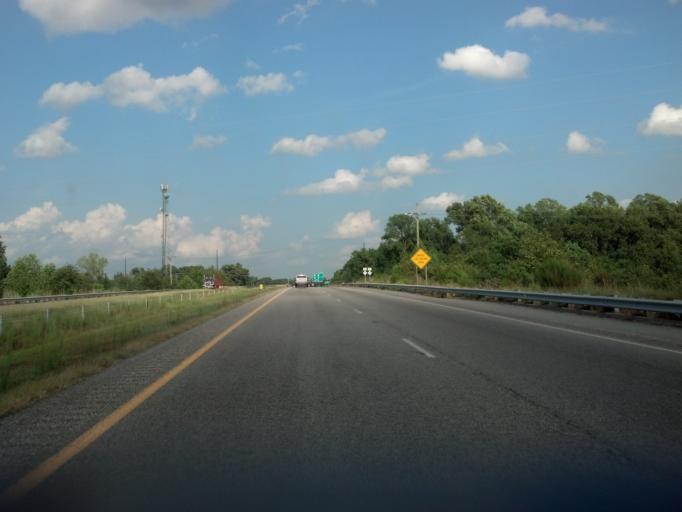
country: US
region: North Carolina
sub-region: Edgecombe County
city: Tarboro
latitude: 35.8842
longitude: -77.5566
